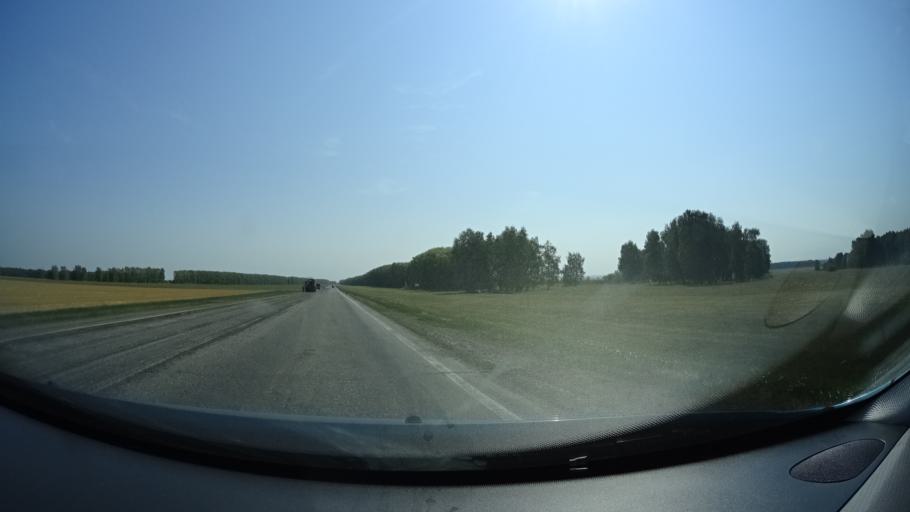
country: RU
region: Bashkortostan
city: Karmaskaly
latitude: 54.3996
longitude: 56.0961
